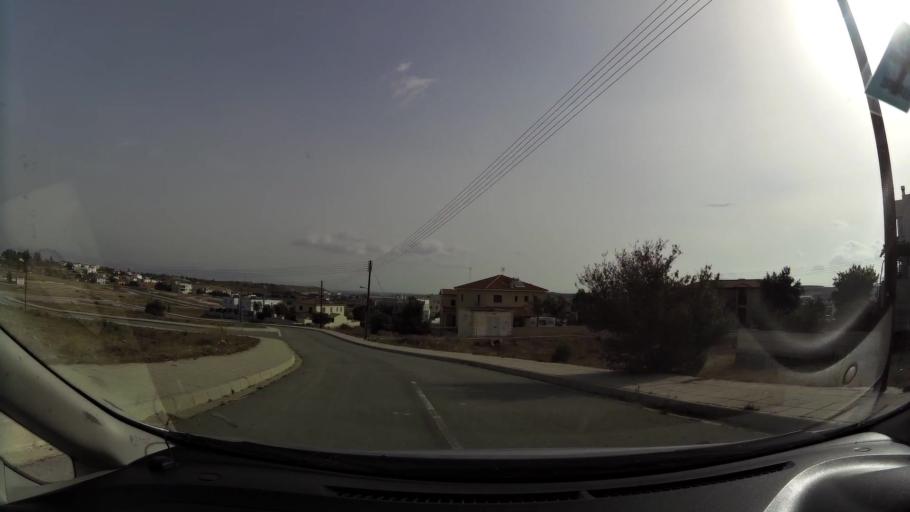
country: CY
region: Lefkosia
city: Geri
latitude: 35.0751
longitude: 33.3928
